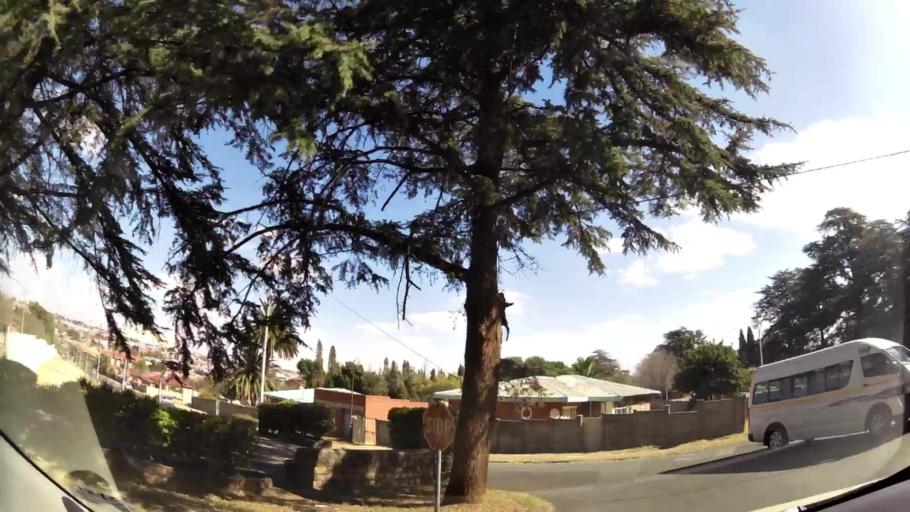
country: ZA
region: Gauteng
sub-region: West Rand District Municipality
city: Krugersdorp
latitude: -26.0974
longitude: 27.7829
